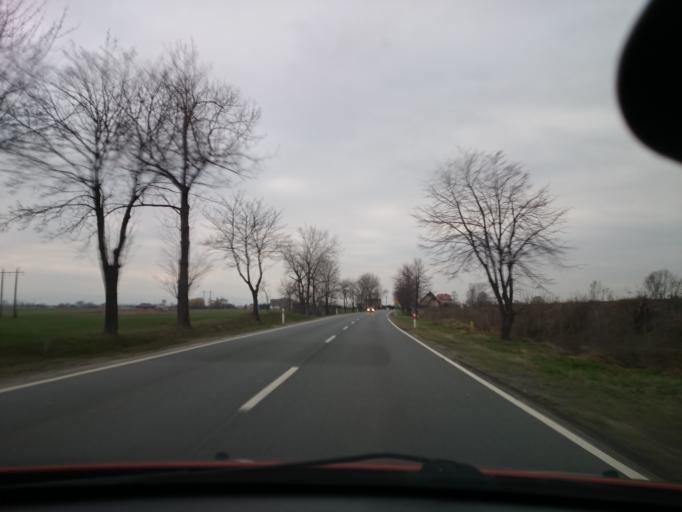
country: PL
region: Opole Voivodeship
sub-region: Powiat nyski
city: Otmuchow
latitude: 50.4681
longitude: 17.2264
